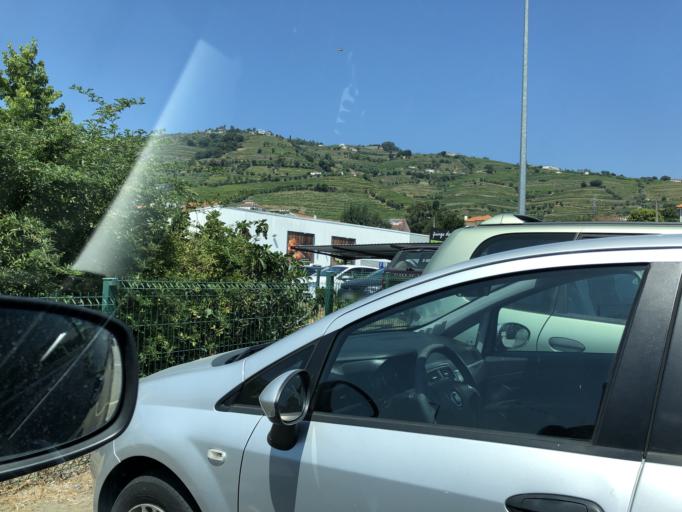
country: PT
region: Vila Real
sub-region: Peso da Regua
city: Godim
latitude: 41.1678
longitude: -7.8023
